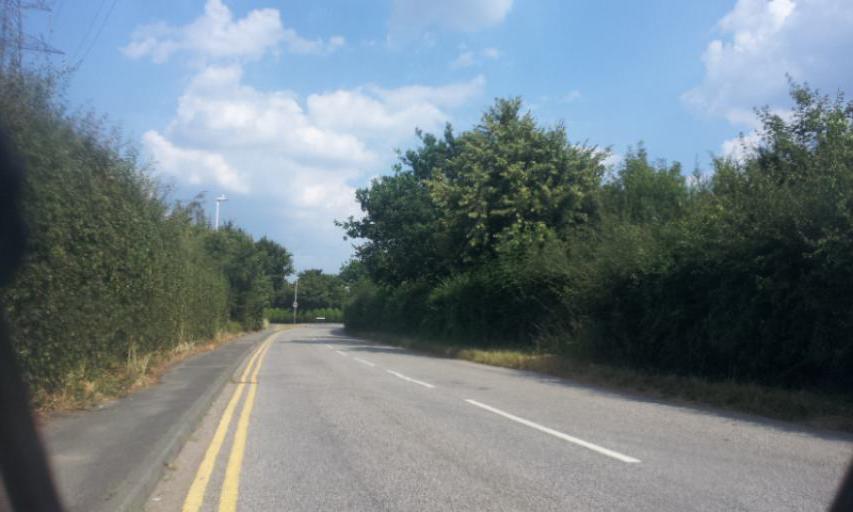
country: GB
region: England
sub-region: Kent
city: Paddock Wood
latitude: 51.1714
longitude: 0.3881
